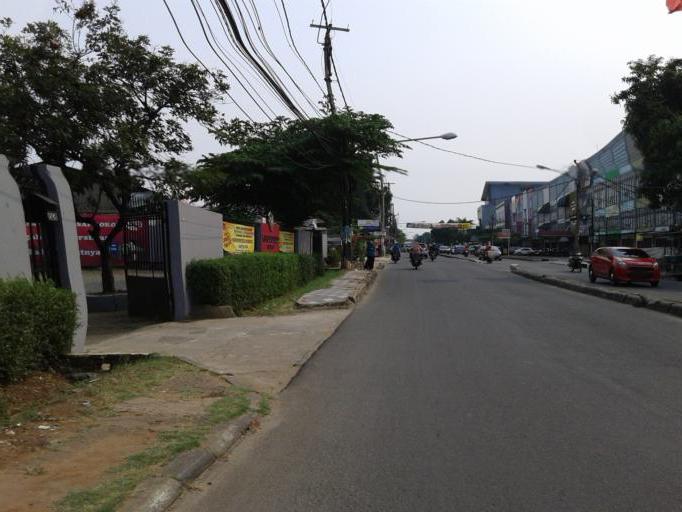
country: ID
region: West Java
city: Pamulang
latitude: -6.3397
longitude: 106.7802
